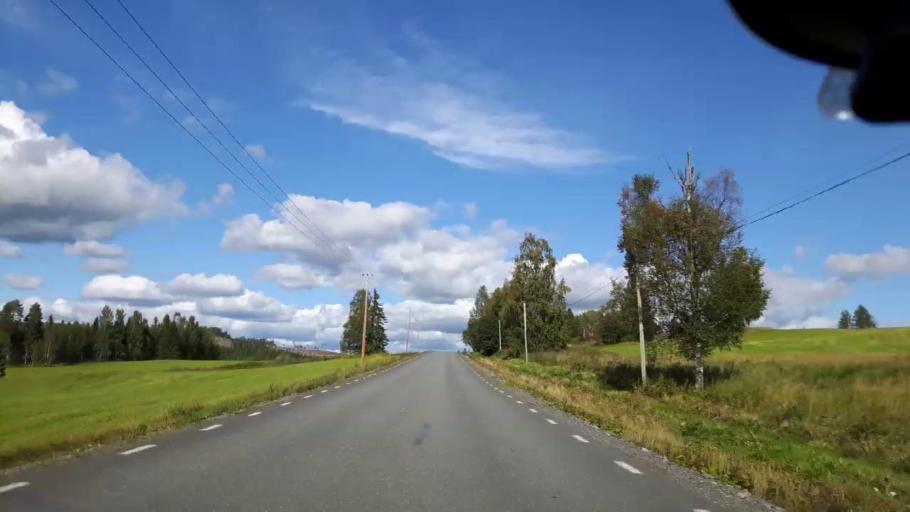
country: SE
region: Jaemtland
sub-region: Braecke Kommun
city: Braecke
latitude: 63.1862
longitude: 15.5594
